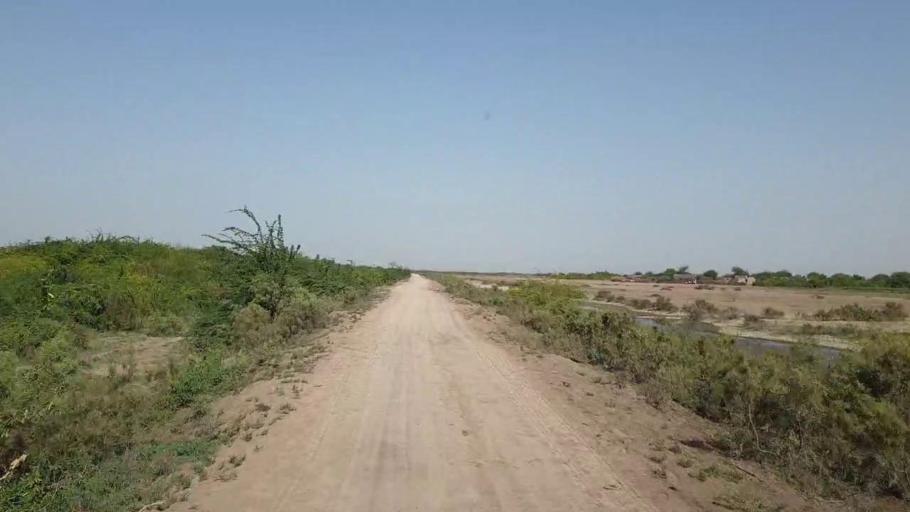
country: PK
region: Sindh
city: Tando Bago
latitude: 24.6477
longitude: 69.0716
